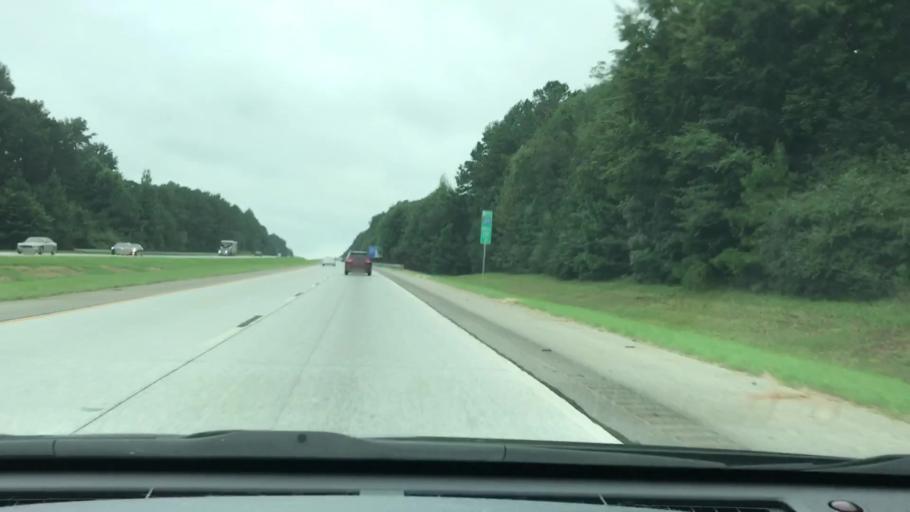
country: US
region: Georgia
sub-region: Morgan County
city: Madison
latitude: 33.5556
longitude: -83.4381
